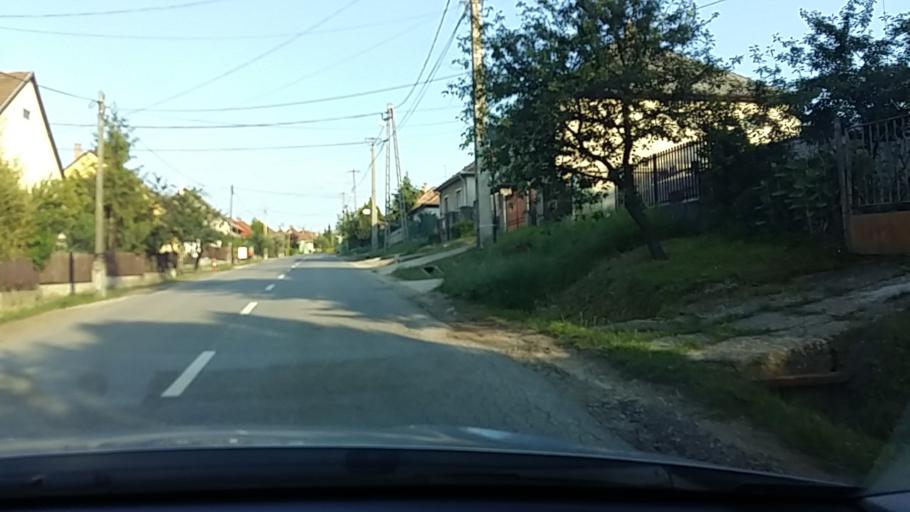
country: HU
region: Pest
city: Szod
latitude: 47.7410
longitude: 19.2192
